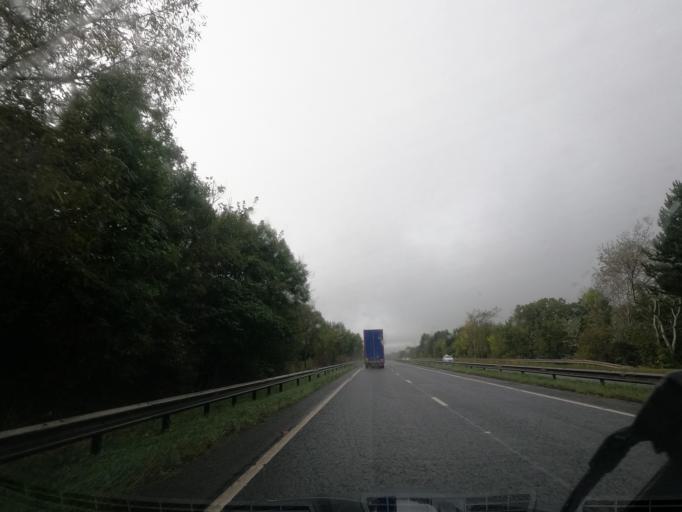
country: GB
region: England
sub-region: Redcar and Cleveland
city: South Bank
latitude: 54.5450
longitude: -1.1634
